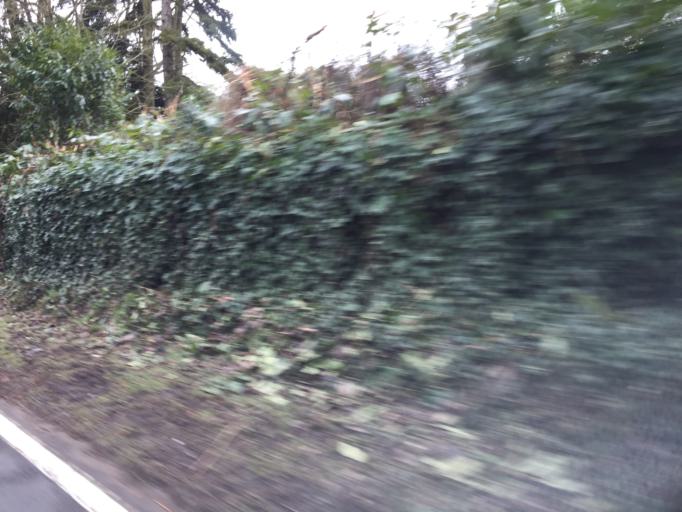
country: GB
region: England
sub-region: West Berkshire
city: Basildon
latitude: 51.5032
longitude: -1.1213
